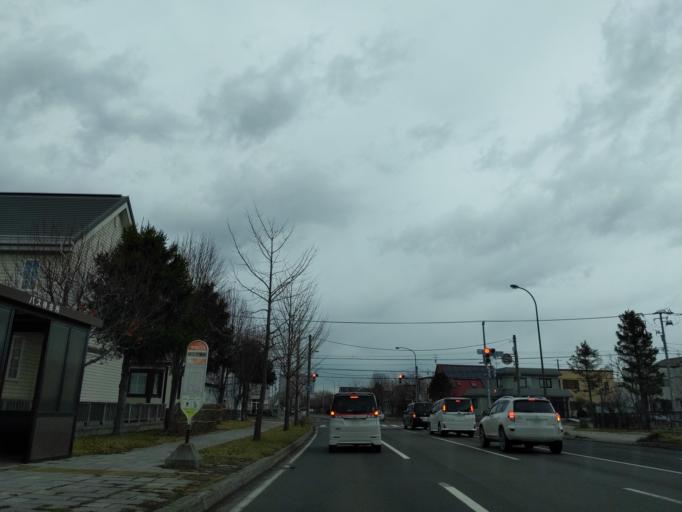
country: JP
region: Hokkaido
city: Sapporo
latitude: 43.1467
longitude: 141.3731
